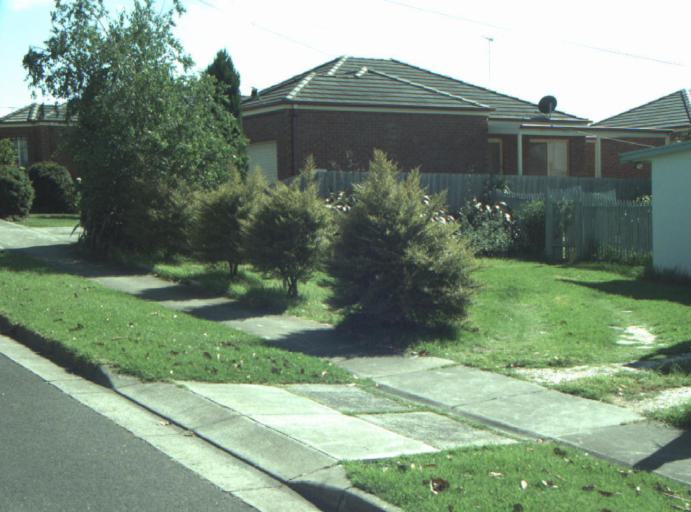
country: AU
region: Victoria
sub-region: Greater Geelong
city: Wandana Heights
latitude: -38.1695
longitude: 144.3137
